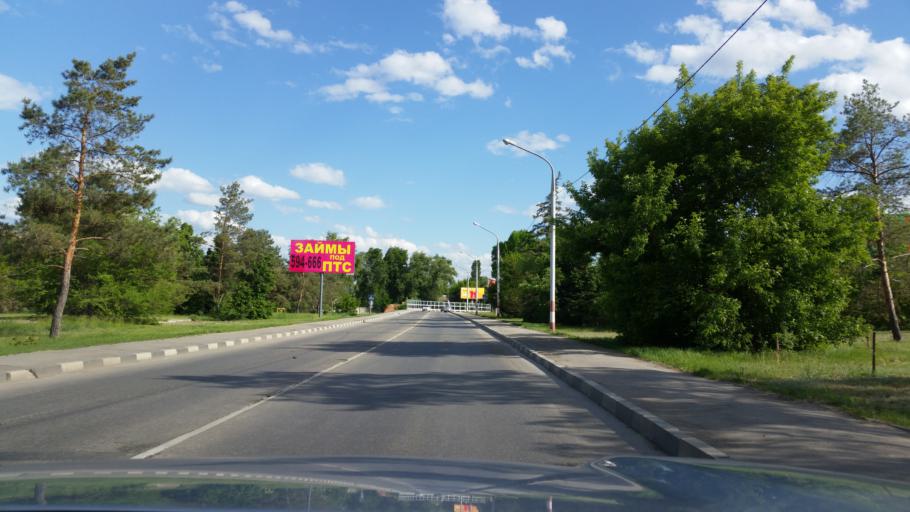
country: RU
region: Saratov
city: Engel's
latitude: 51.5045
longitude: 46.0795
